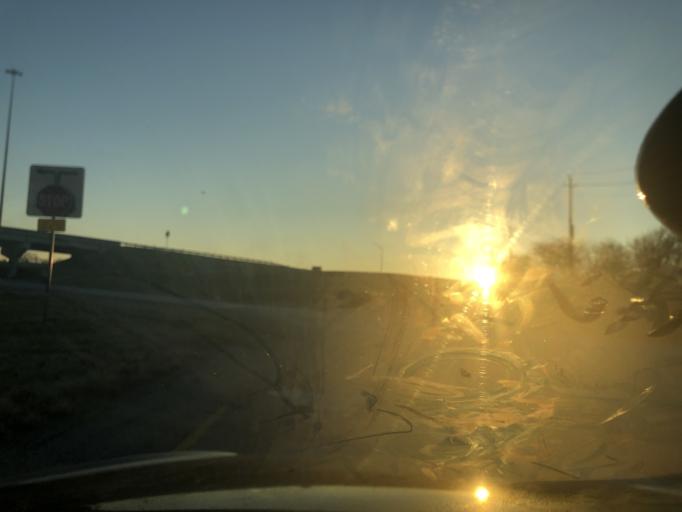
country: US
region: Texas
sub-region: Tarrant County
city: White Settlement
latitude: 32.7397
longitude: -97.4833
